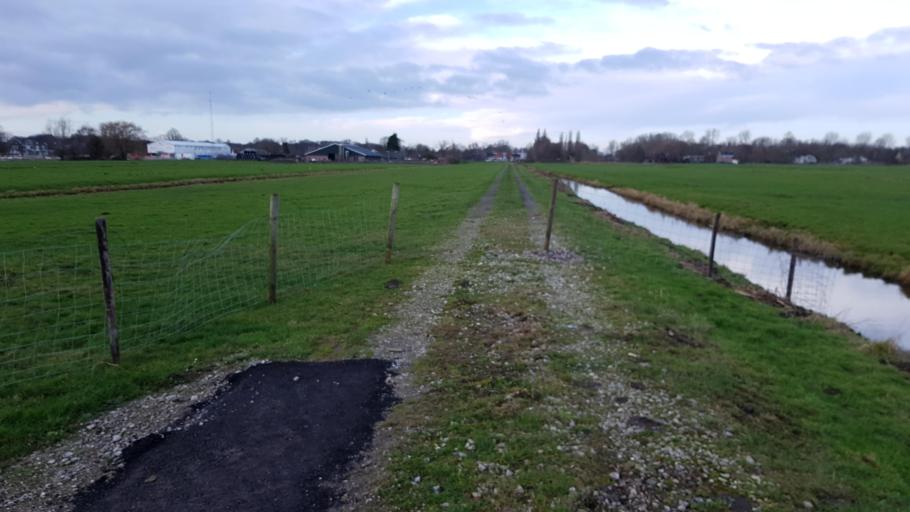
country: NL
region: South Holland
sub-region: Gemeente Voorschoten
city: Voorschoten
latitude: 52.1284
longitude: 4.4730
